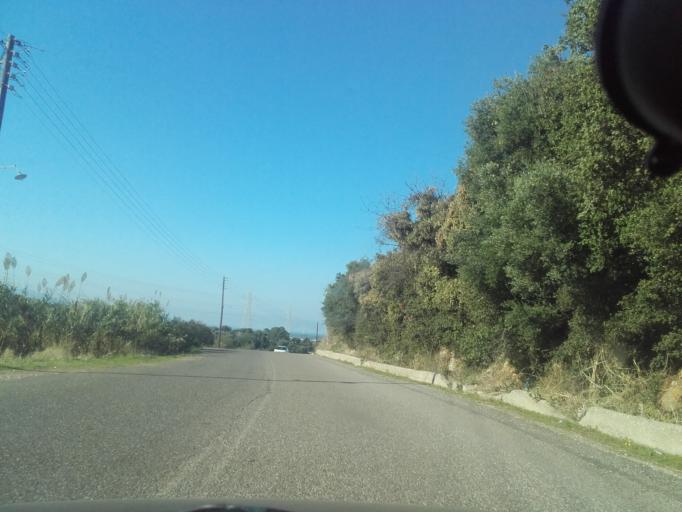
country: GR
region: West Greece
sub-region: Nomos Aitolias kai Akarnanias
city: Nafpaktos
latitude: 38.4168
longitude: 21.9035
